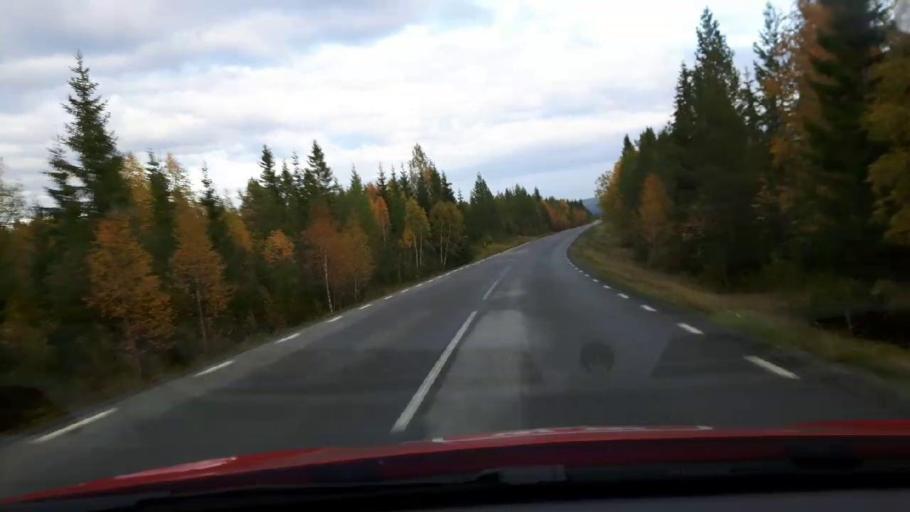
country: SE
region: Jaemtland
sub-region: OEstersunds Kommun
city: Ostersund
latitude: 63.3258
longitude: 14.6238
